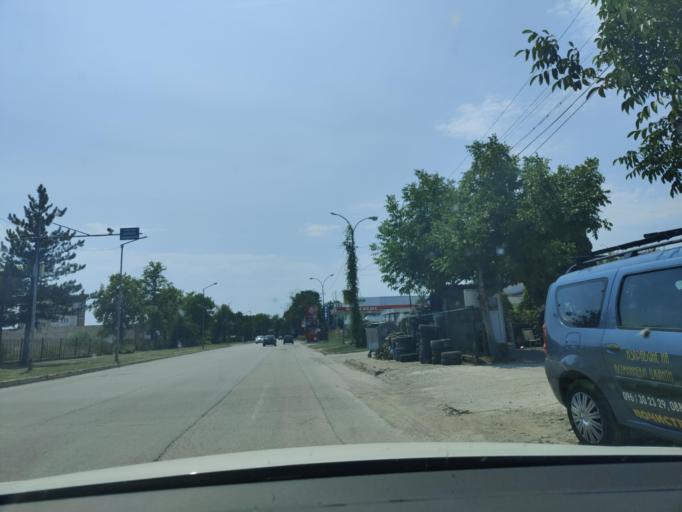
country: BG
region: Montana
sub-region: Obshtina Montana
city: Montana
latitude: 43.4298
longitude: 23.2306
